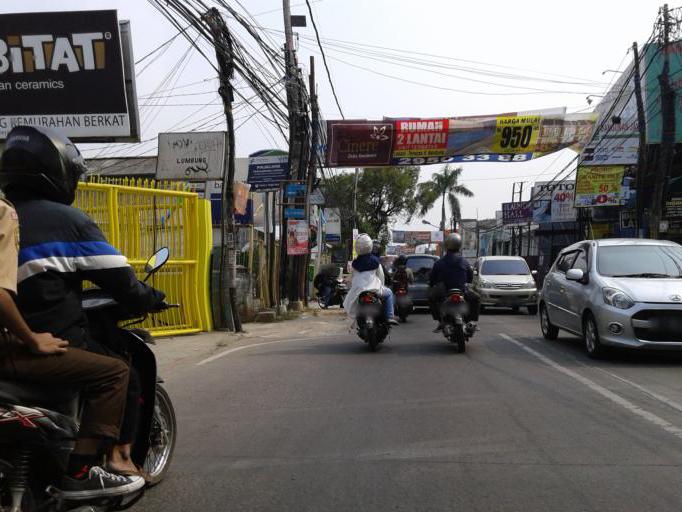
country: ID
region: West Java
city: Pamulang
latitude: -6.3348
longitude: 106.7824
